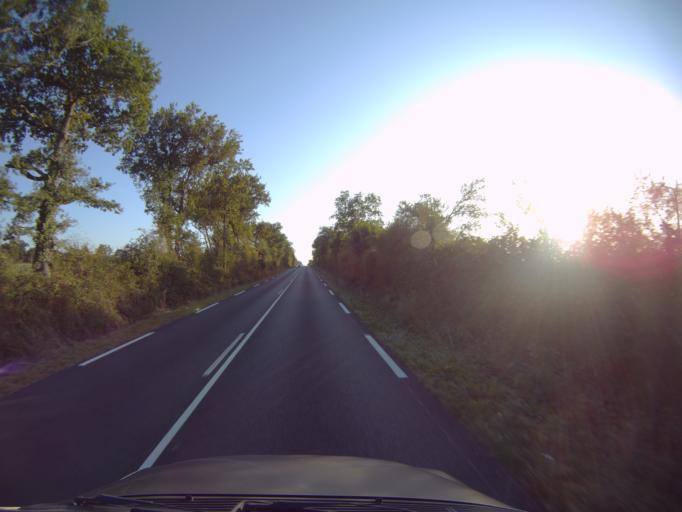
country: FR
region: Pays de la Loire
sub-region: Departement de la Vendee
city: Montaigu
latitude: 46.9949
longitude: -1.2943
